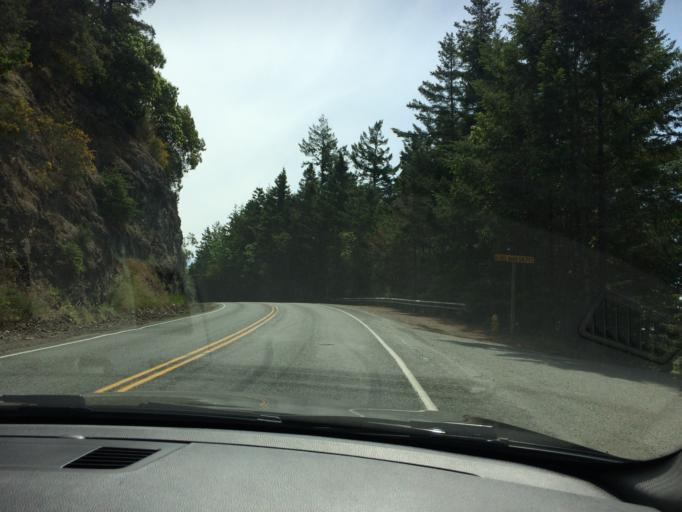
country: US
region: Washington
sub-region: Skagit County
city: Anacortes
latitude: 48.4775
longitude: -122.6614
